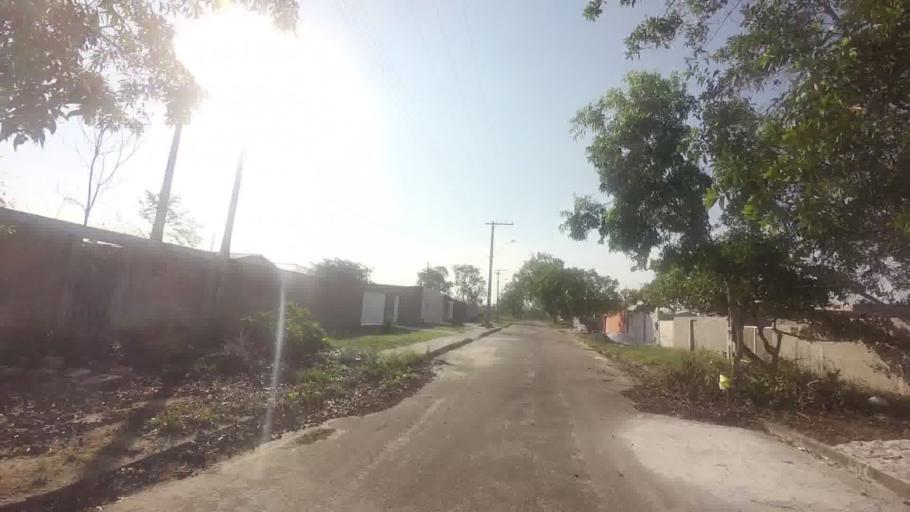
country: BR
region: Espirito Santo
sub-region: Guarapari
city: Guarapari
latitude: -20.7261
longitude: -40.5377
